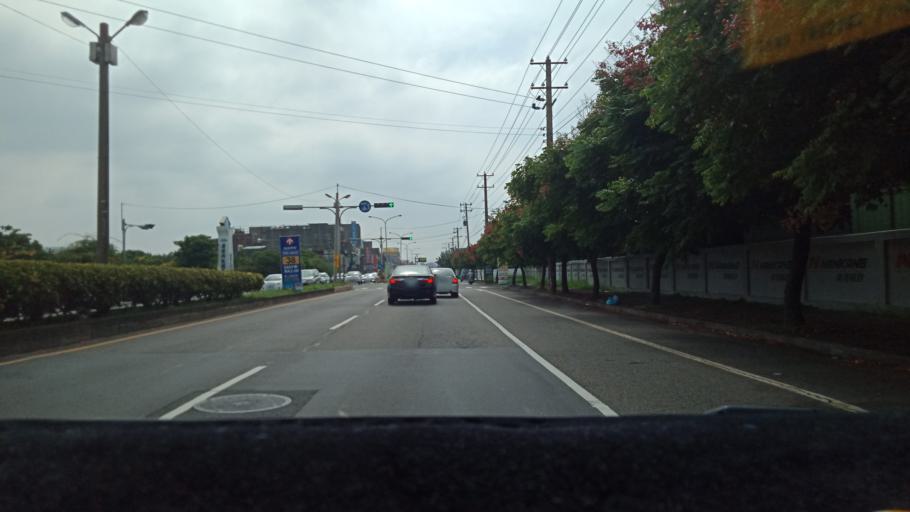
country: TW
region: Taiwan
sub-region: Hsinchu
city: Zhubei
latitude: 24.8764
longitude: 121.0042
